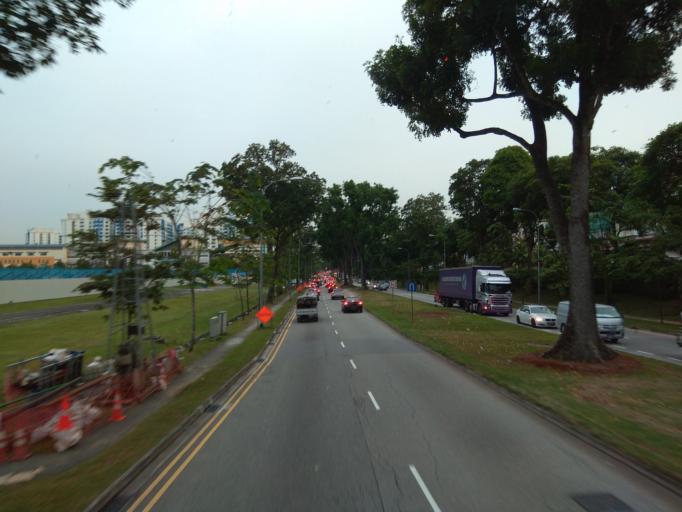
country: MY
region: Johor
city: Johor Bahru
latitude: 1.3545
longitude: 103.6988
